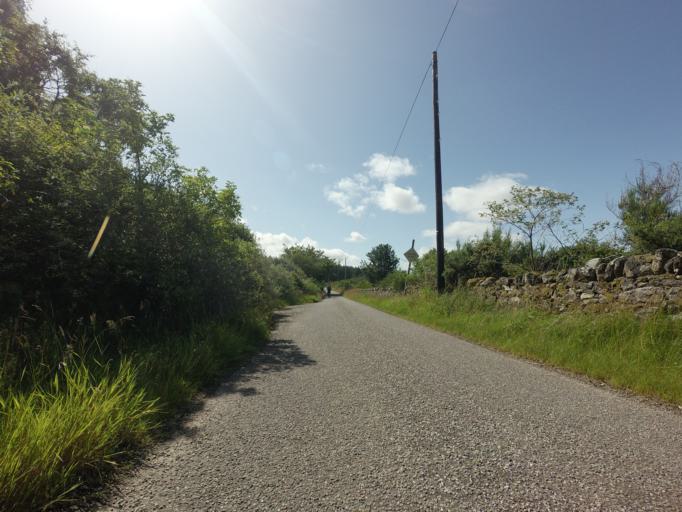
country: GB
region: Scotland
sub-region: Highland
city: Nairn
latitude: 57.5024
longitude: -3.9388
